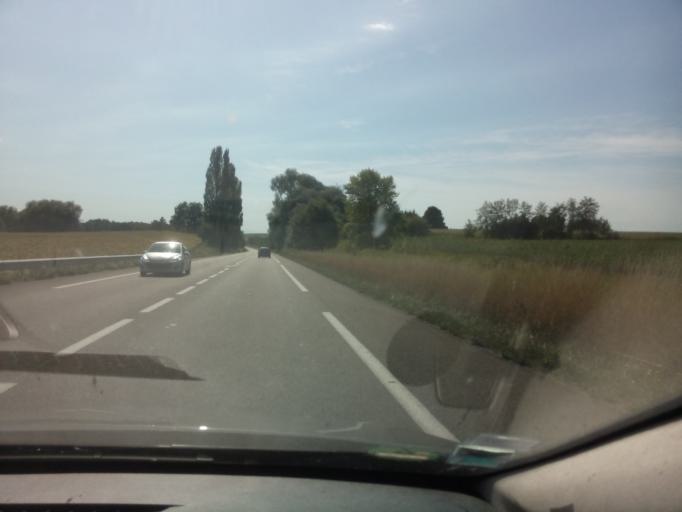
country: FR
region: Alsace
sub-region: Departement du Bas-Rhin
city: Soultz-sous-Forets
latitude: 48.9195
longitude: 7.8861
